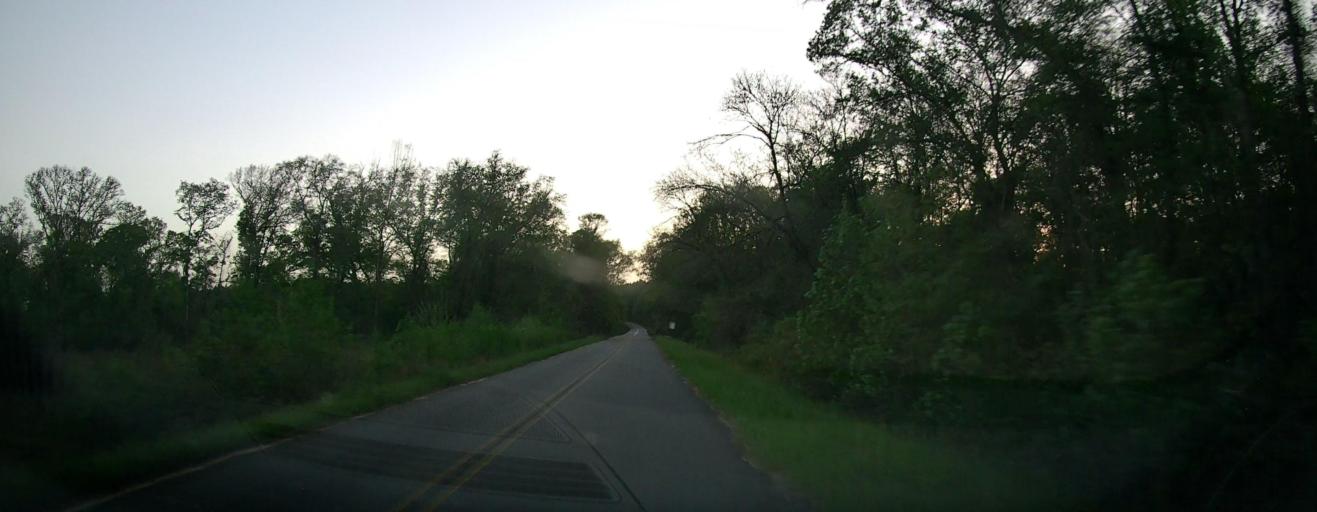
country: US
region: Georgia
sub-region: Marion County
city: Buena Vista
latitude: 32.2568
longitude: -84.5757
